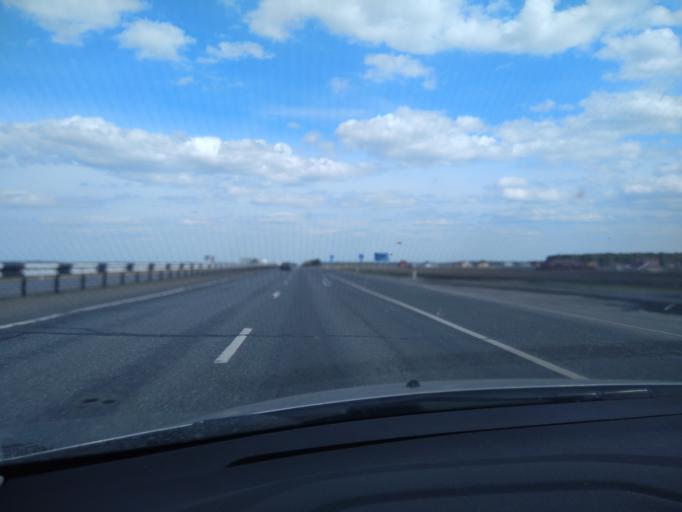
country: RU
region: Tjumen
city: Moskovskiy
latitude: 57.0942
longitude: 65.1686
